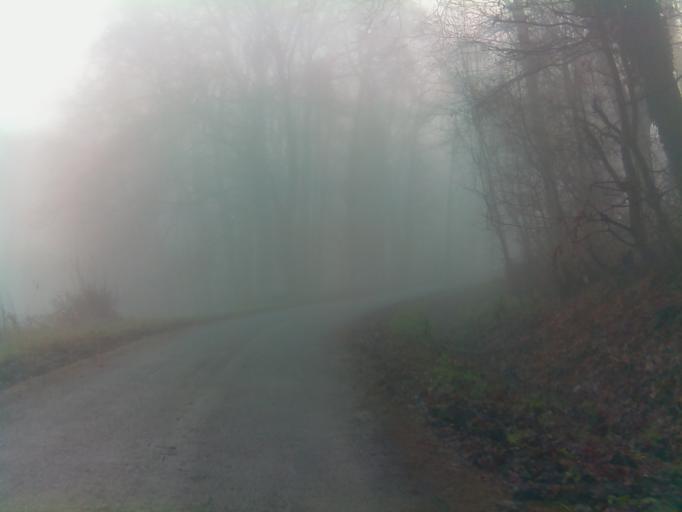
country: DE
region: Bavaria
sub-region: Regierungsbezirk Unterfranken
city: Kreuzwertheim
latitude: 49.7589
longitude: 9.5394
